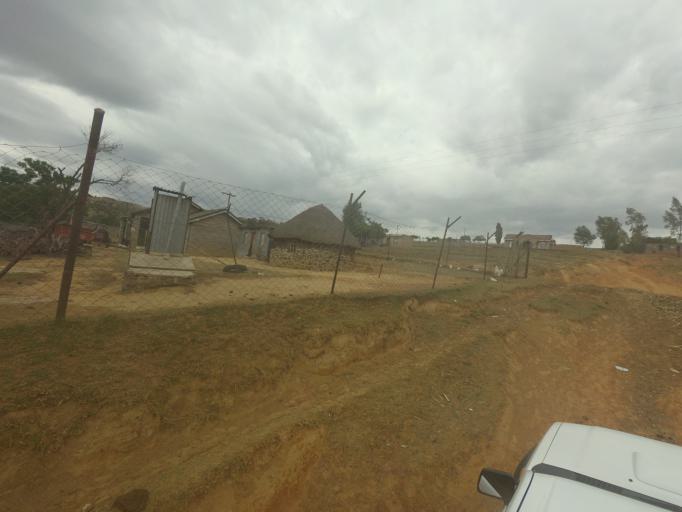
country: LS
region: Leribe
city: Leribe
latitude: -29.0259
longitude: 28.0189
